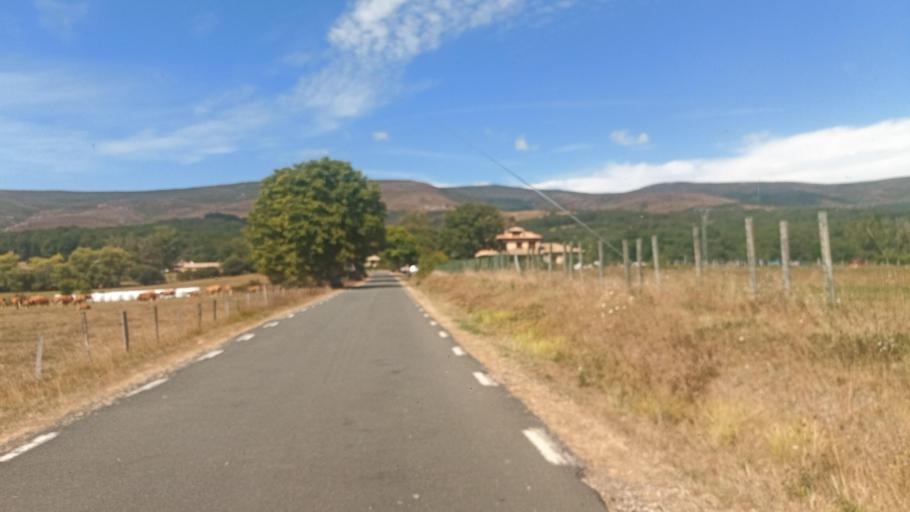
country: ES
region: Castille and Leon
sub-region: Provincia de Burgos
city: Espinosa de los Monteros
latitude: 43.0442
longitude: -3.6691
